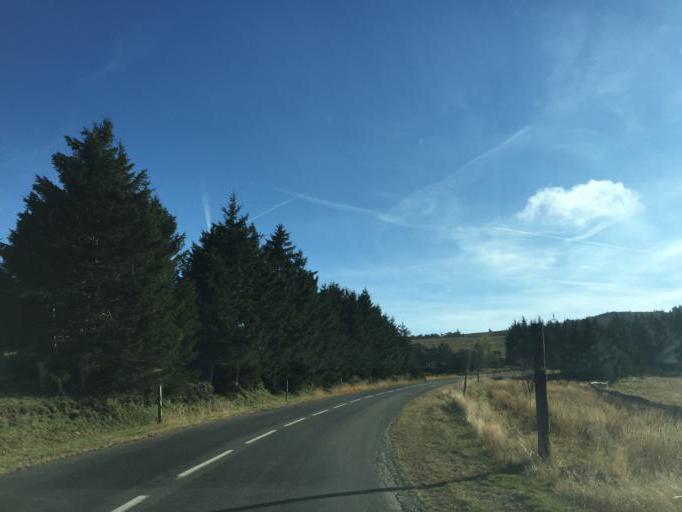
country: FR
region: Rhone-Alpes
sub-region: Departement de la Loire
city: Saint-Julien-Molin-Molette
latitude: 45.3881
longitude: 4.5763
